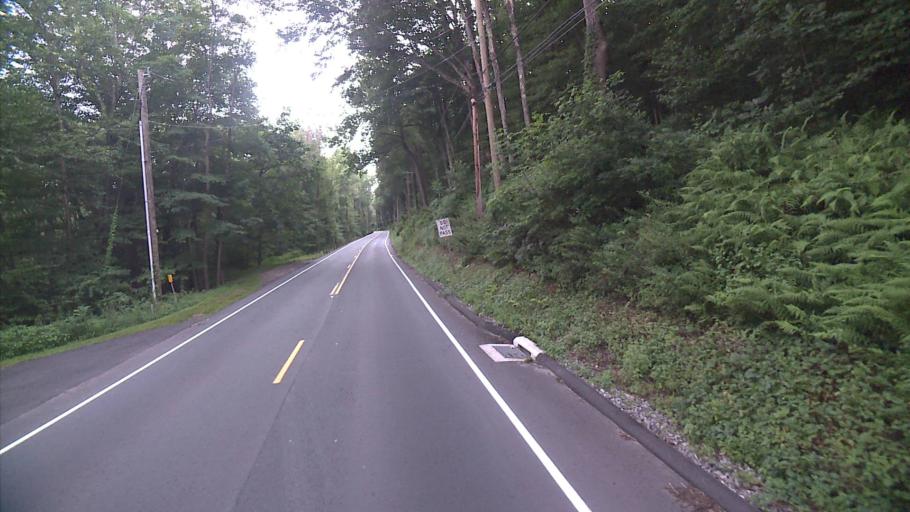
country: US
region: Connecticut
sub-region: New Haven County
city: Heritage Village
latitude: 41.5260
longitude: -73.2700
